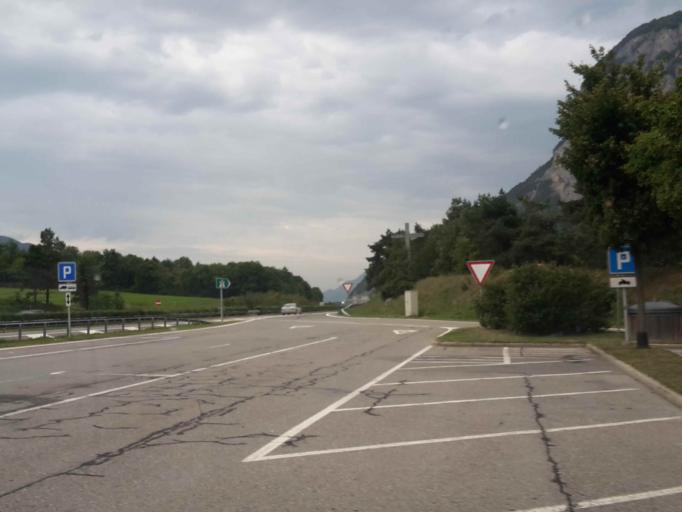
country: CH
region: Valais
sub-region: Martigny District
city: Evionnaz
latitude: 46.1844
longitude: 7.0264
